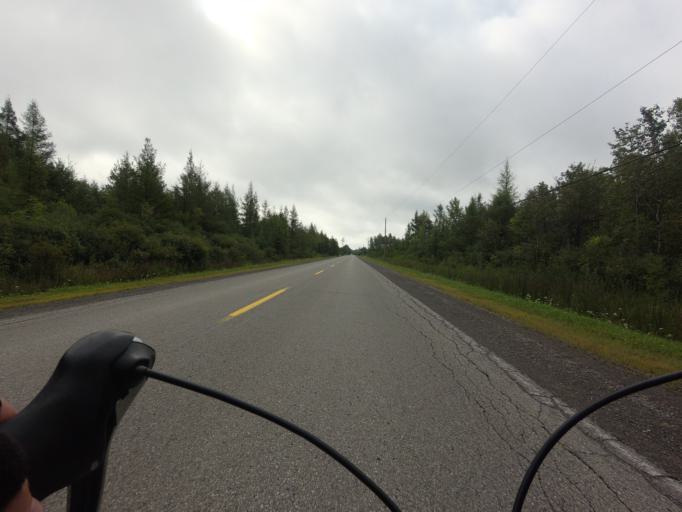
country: CA
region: Ontario
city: Bells Corners
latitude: 45.0739
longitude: -75.7368
